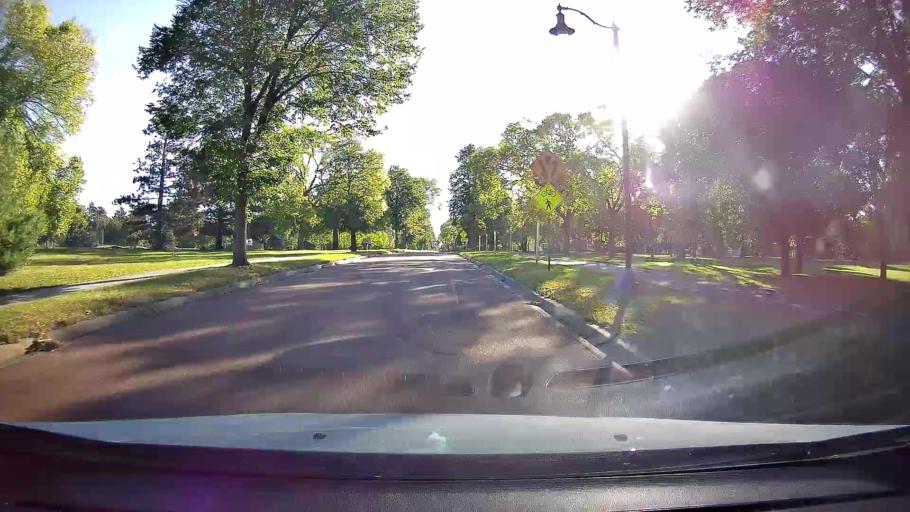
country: US
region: Minnesota
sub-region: Hennepin County
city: Richfield
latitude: 44.9164
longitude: -93.2366
